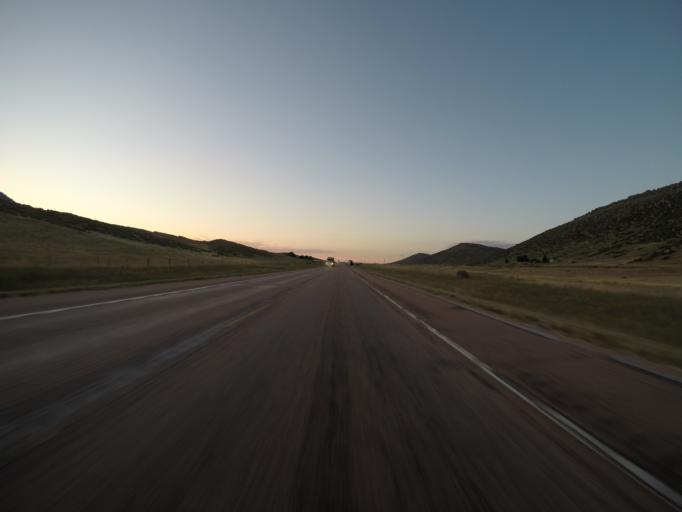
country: US
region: Colorado
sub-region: Larimer County
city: Laporte
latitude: 40.7245
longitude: -105.1717
